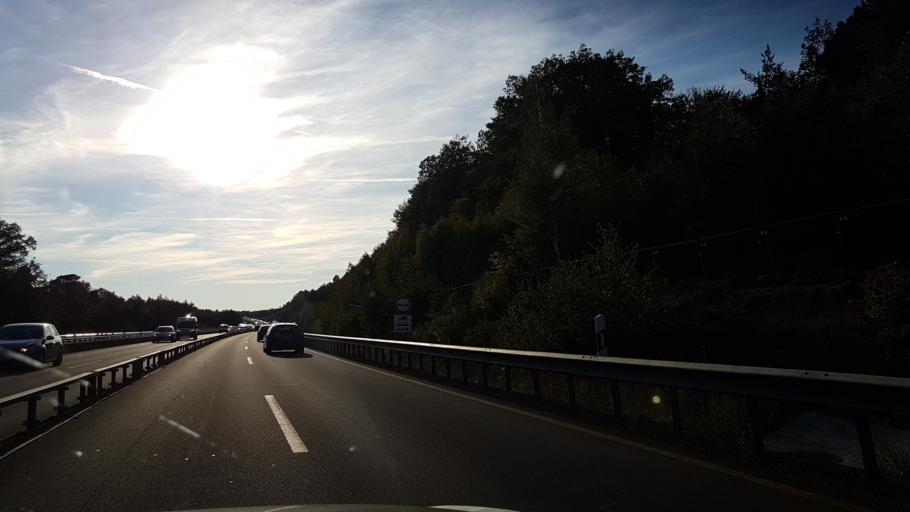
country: DE
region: Rheinland-Pfalz
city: Otterbach
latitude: 49.4497
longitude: 7.7228
